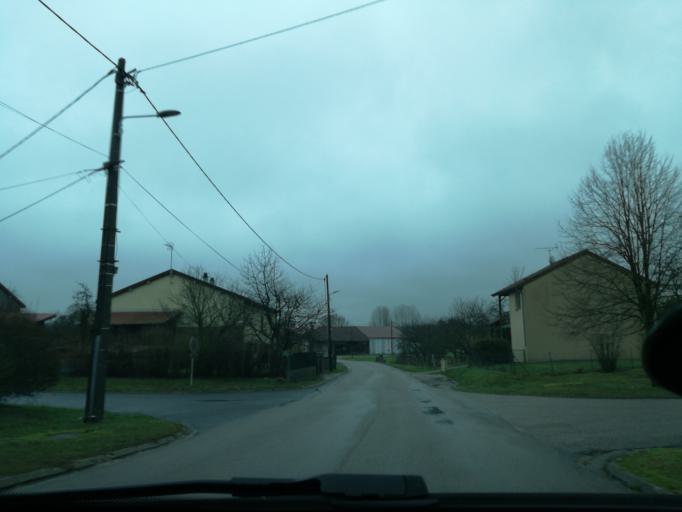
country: FR
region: Lorraine
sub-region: Departement de la Meuse
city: Clermont-en-Argonne
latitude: 49.0203
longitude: 5.1071
